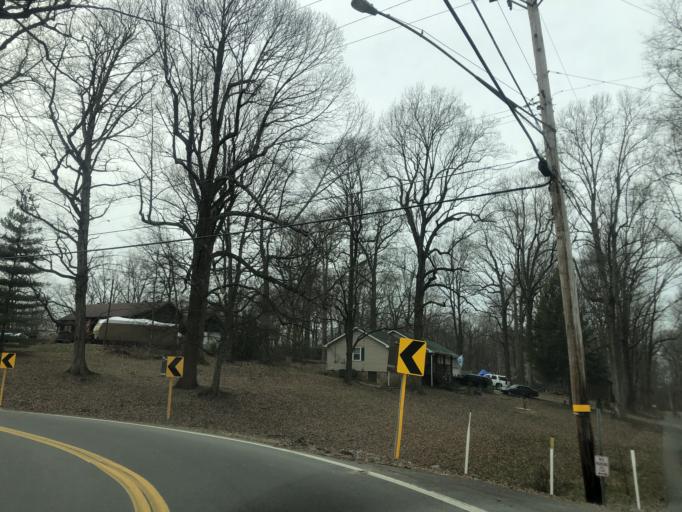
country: US
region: Tennessee
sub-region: Robertson County
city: Ridgetop
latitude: 36.3963
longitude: -86.7792
